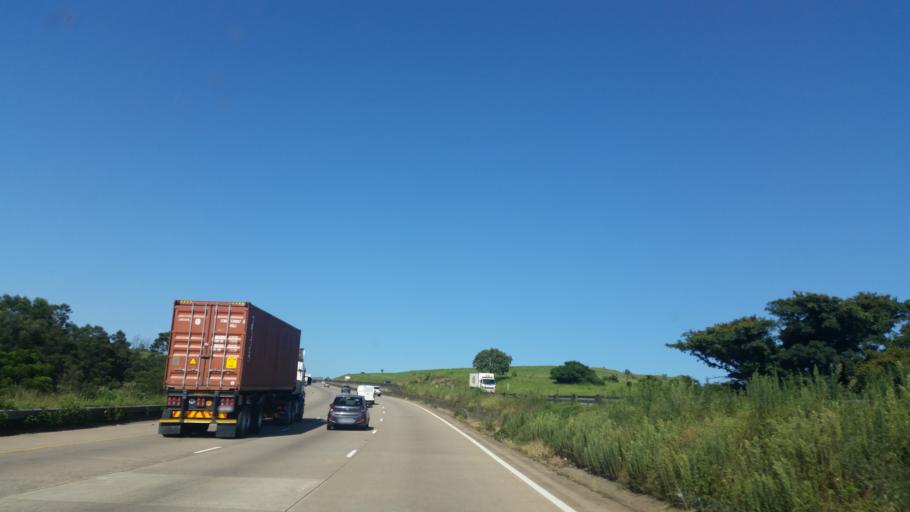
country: ZA
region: KwaZulu-Natal
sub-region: eThekwini Metropolitan Municipality
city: Mpumalanga
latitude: -29.7369
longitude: 30.6439
